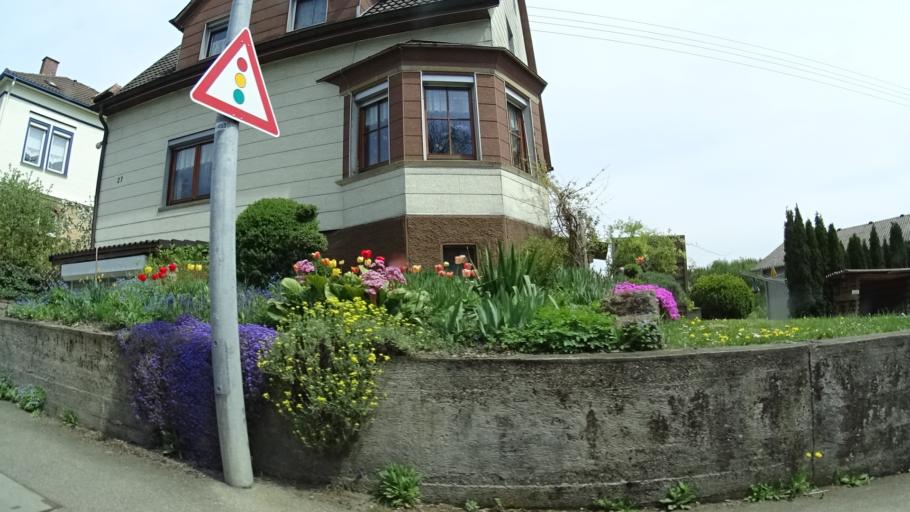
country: DE
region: Baden-Wuerttemberg
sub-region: Freiburg Region
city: Rottweil
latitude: 48.1437
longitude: 8.6291
